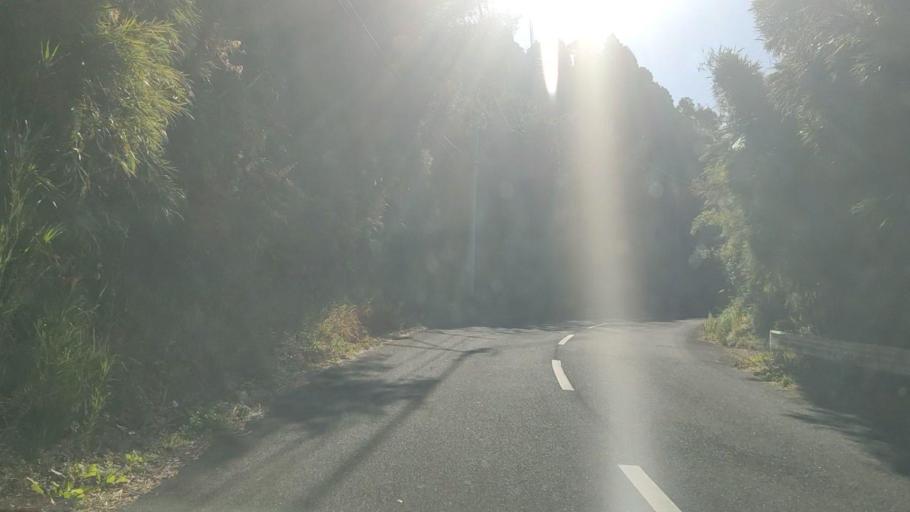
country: JP
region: Kagoshima
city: Kokubu-matsuki
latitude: 31.6671
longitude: 130.8226
